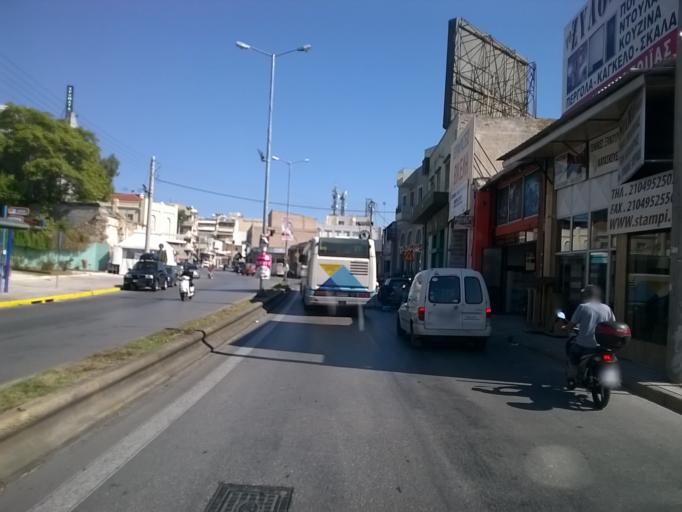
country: GR
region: Attica
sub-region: Nomos Piraios
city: Nikaia
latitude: 37.9551
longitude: 23.6492
